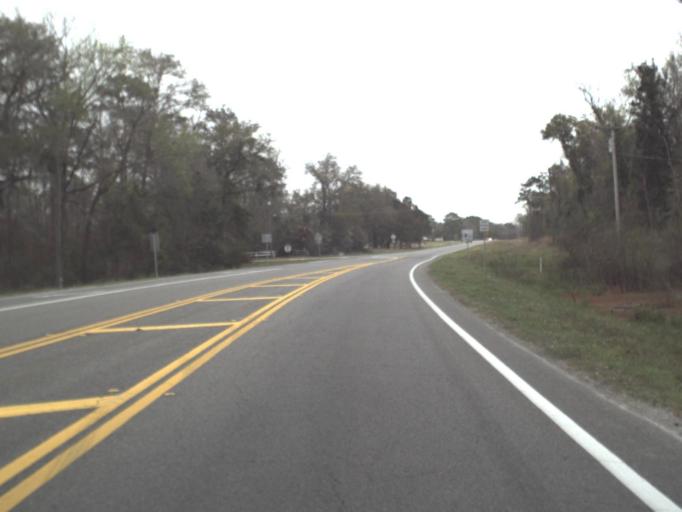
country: US
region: Florida
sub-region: Wakulla County
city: Crawfordville
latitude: 30.1275
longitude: -84.3634
